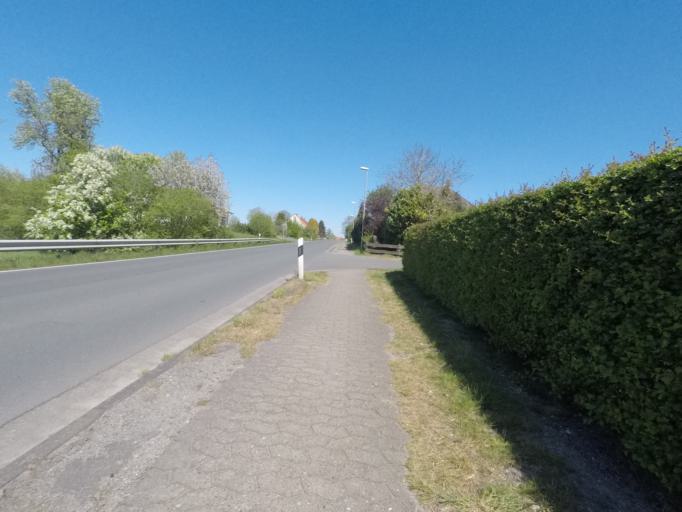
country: DE
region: North Rhine-Westphalia
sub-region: Regierungsbezirk Detmold
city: Leopoldshohe
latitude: 52.0601
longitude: 8.6786
